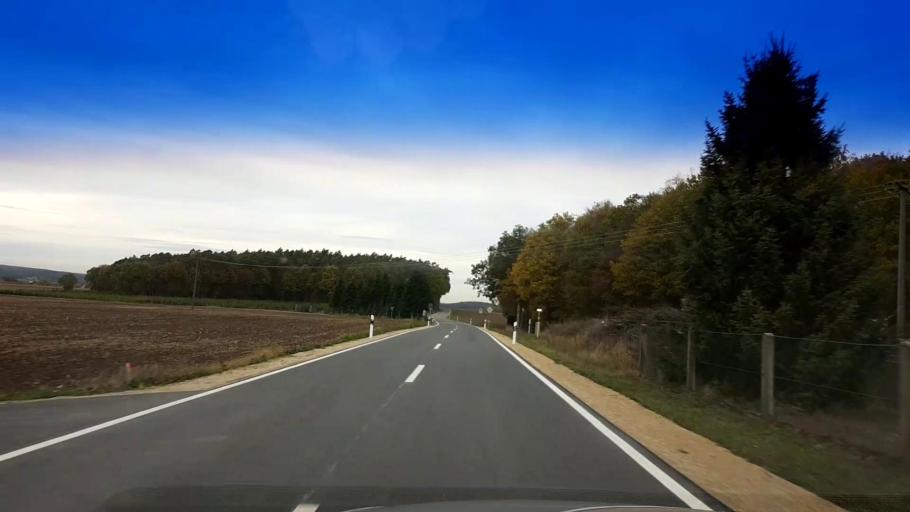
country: DE
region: Bavaria
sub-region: Upper Franconia
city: Priesendorf
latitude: 49.9216
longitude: 10.7153
